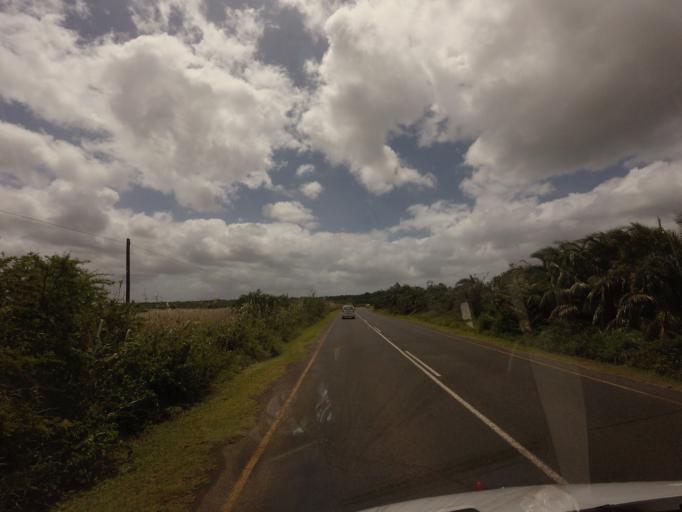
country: ZA
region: KwaZulu-Natal
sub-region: uMkhanyakude District Municipality
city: Mtubatuba
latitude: -28.3706
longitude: 32.4055
